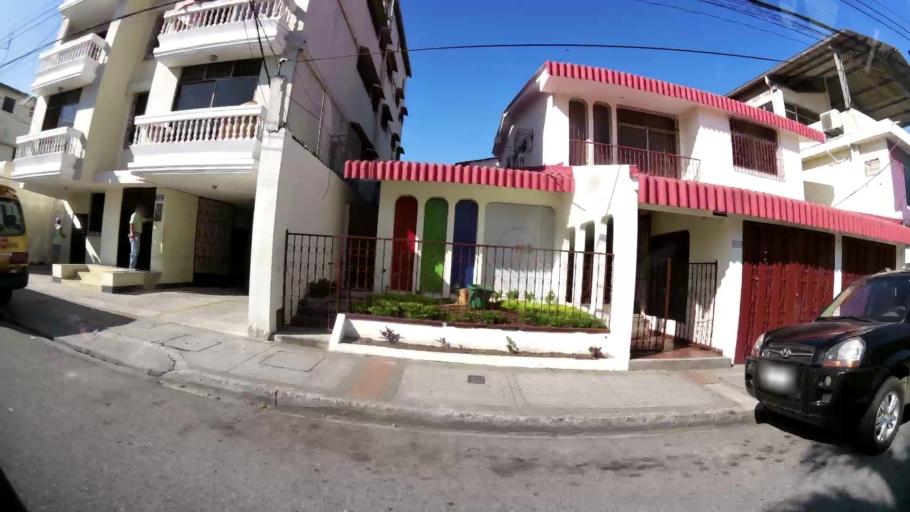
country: EC
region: Guayas
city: Guayaquil
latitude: -2.1750
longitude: -79.8964
